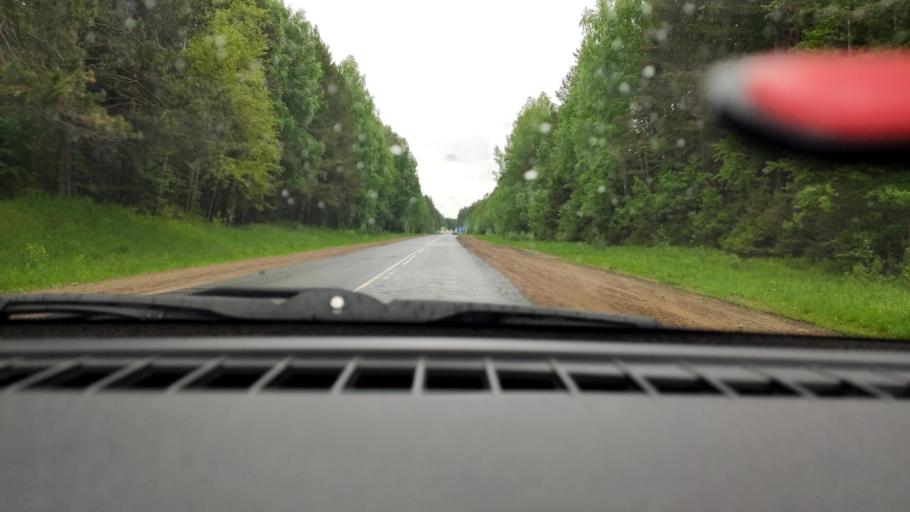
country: RU
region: Perm
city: Karagay
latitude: 58.2545
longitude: 54.8767
